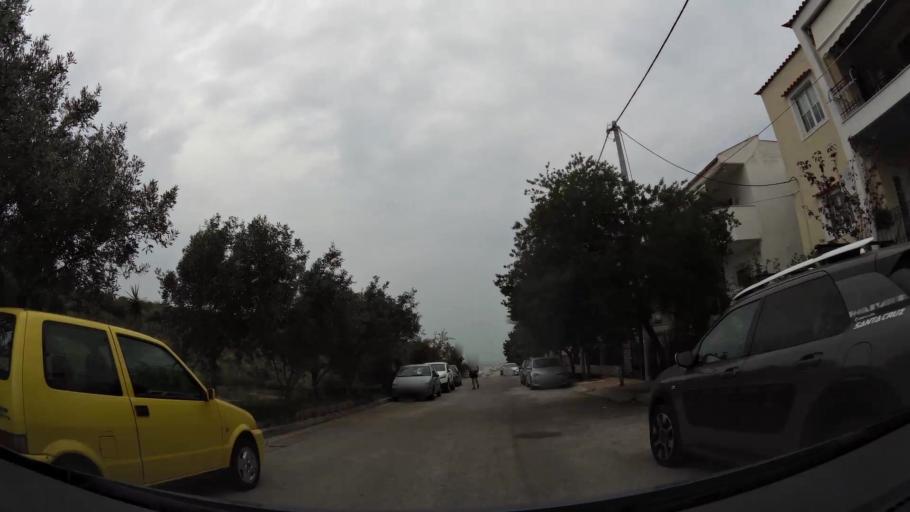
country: GR
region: Attica
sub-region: Nomarchia Athinas
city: Alimos
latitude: 37.9117
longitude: 23.7278
